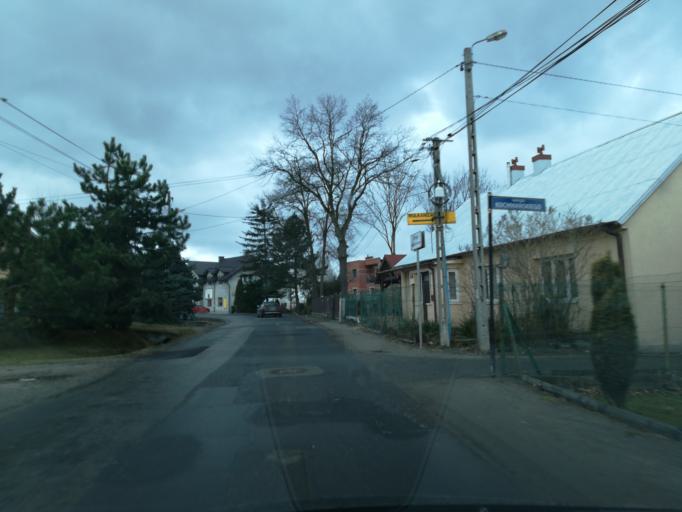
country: PL
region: Lesser Poland Voivodeship
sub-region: Krakow
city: Sidzina
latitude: 49.9906
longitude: 19.8638
